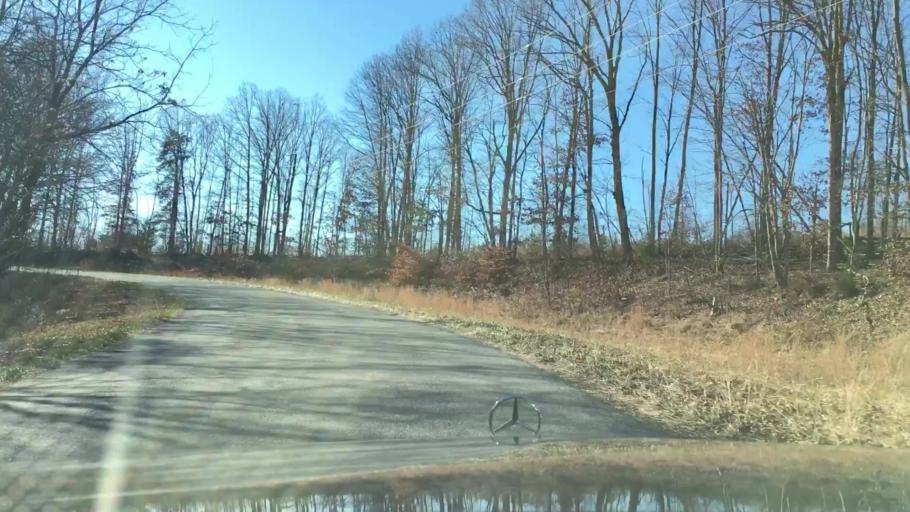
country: US
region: Virginia
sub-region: Campbell County
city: Altavista
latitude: 37.1661
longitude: -79.3599
